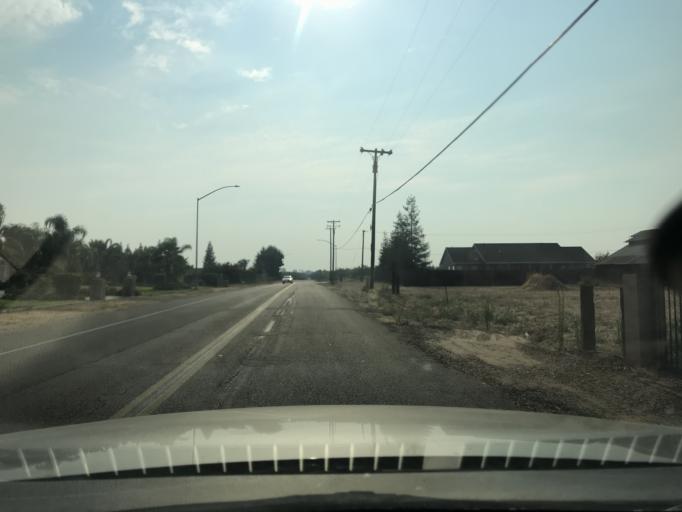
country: US
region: California
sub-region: Merced County
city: Atwater
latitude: 37.3240
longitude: -120.5992
